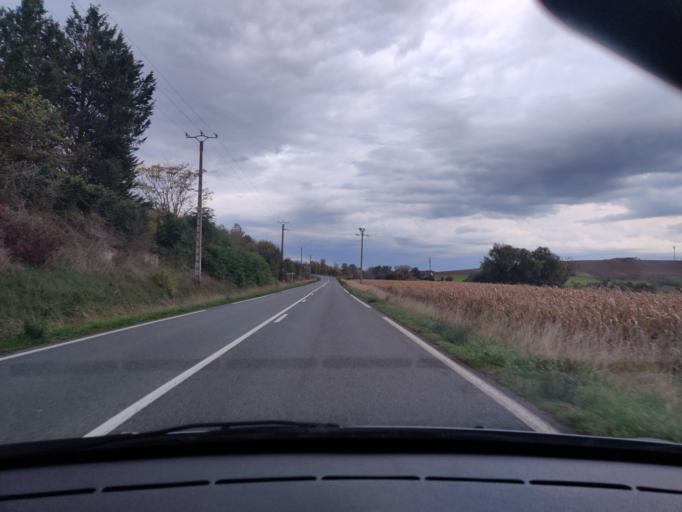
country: FR
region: Auvergne
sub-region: Departement du Puy-de-Dome
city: Combronde
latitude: 45.9697
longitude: 3.1025
